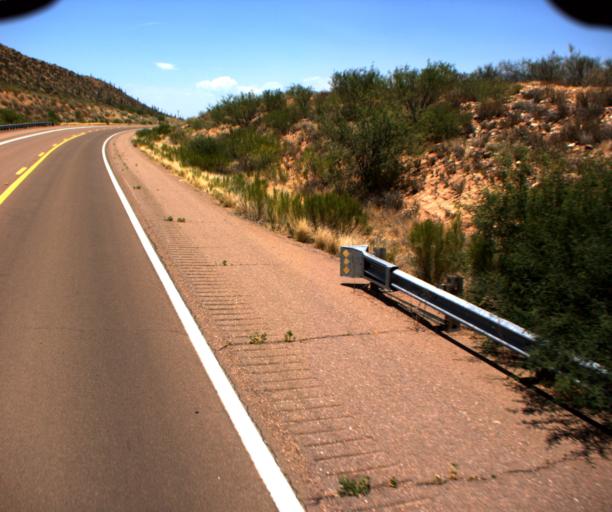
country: US
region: Arizona
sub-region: Gila County
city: Tonto Basin
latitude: 33.8985
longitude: -111.3104
